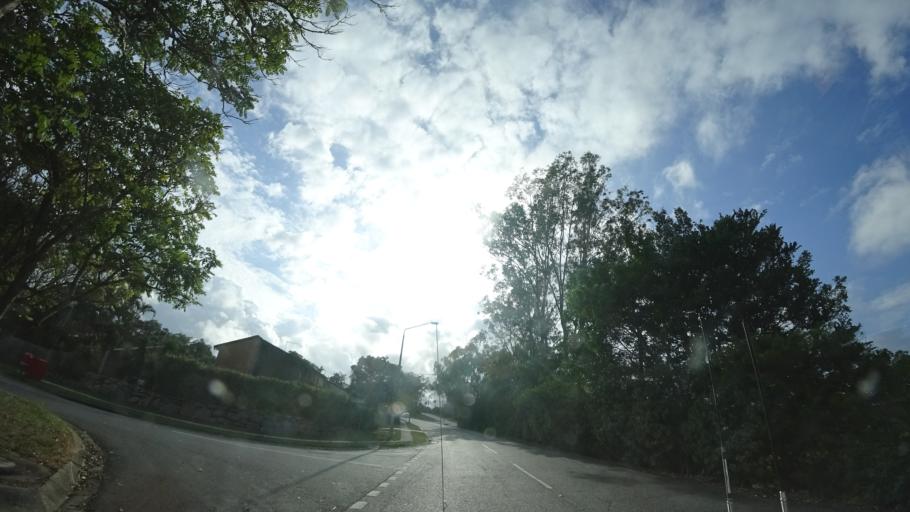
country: AU
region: Queensland
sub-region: Moreton Bay
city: Ferny Hills
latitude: -27.4457
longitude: 152.9315
